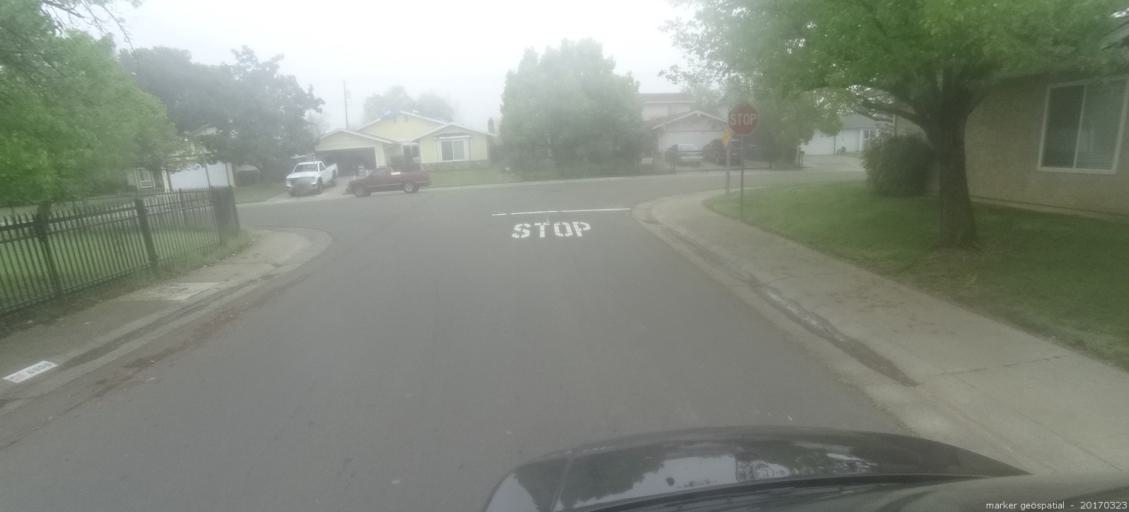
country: US
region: California
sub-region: Sacramento County
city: Florin
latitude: 38.5026
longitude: -121.4155
